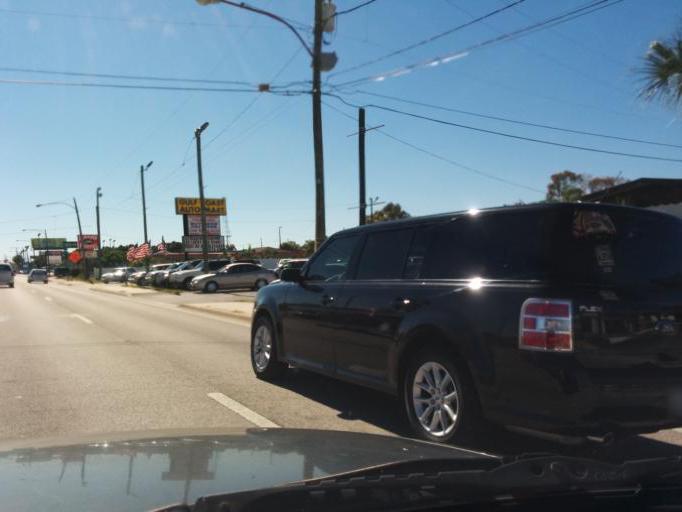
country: US
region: Florida
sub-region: Pinellas County
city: Lealman
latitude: 27.8165
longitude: -82.6796
